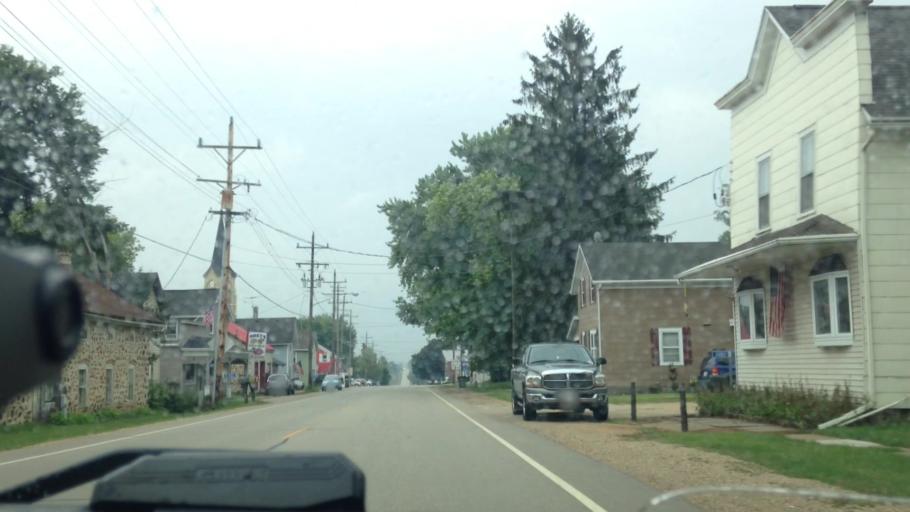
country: US
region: Wisconsin
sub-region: Washington County
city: Slinger
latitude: 43.3709
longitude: -88.3345
